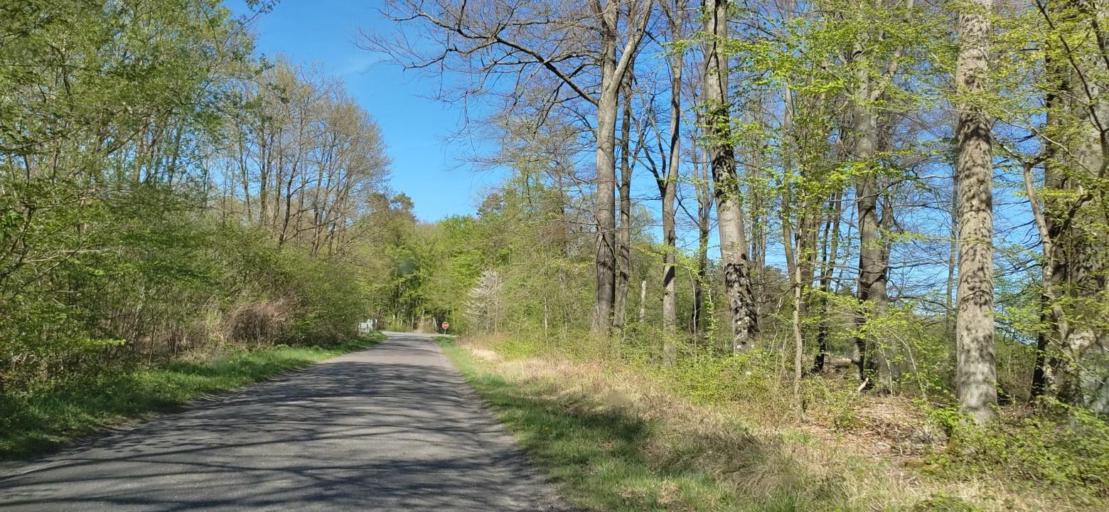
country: FR
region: Picardie
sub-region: Departement de l'Oise
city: Le Plessis-Brion
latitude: 49.4533
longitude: 2.9245
